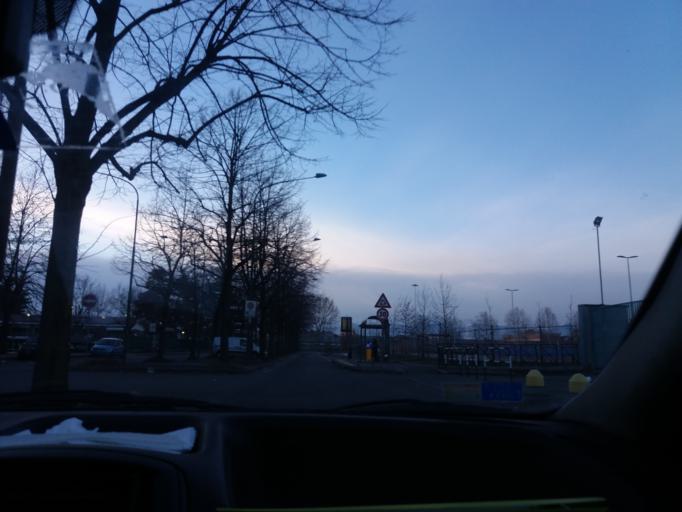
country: IT
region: Piedmont
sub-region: Provincia di Torino
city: Fornaci
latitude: 45.0230
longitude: 7.6089
